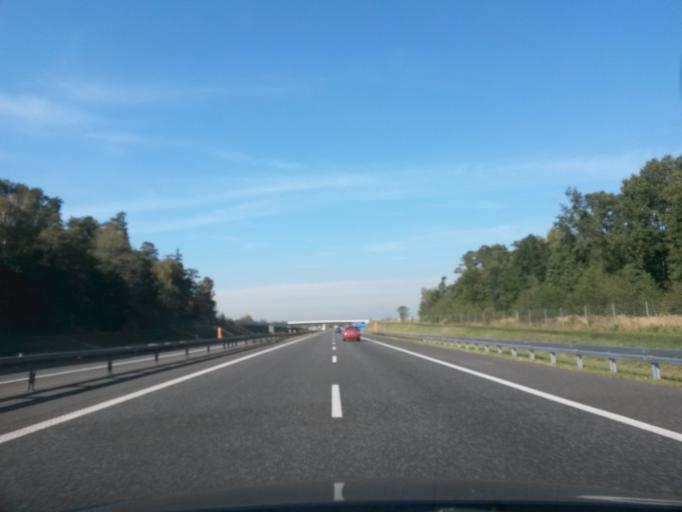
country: PL
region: Silesian Voivodeship
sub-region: Powiat gliwicki
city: Sosnicowice
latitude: 50.3348
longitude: 18.5451
